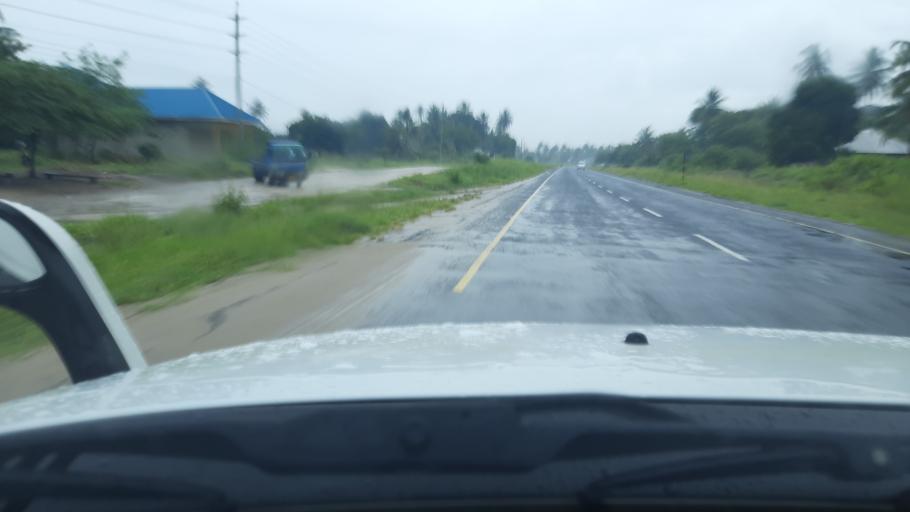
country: TZ
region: Pwani
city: Bagamoyo
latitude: -6.5090
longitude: 38.9317
